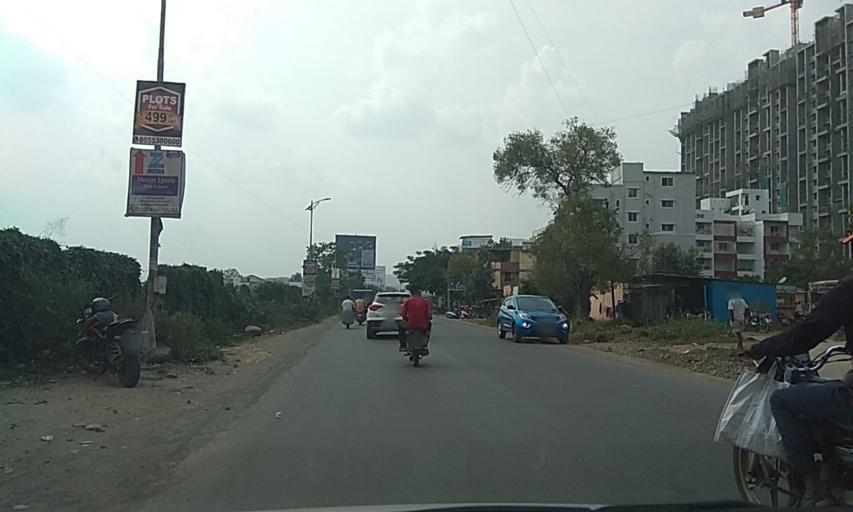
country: IN
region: Maharashtra
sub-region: Pune Division
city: Pimpri
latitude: 18.5835
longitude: 73.7294
